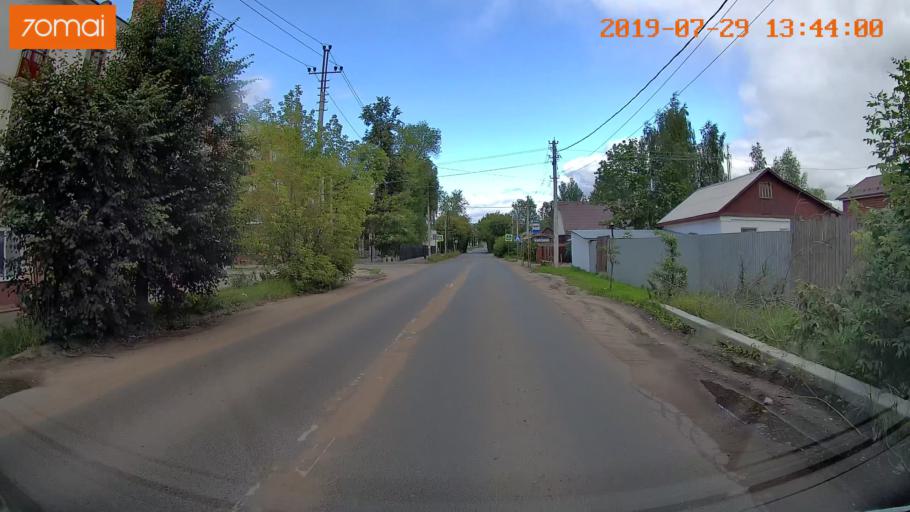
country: RU
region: Ivanovo
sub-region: Gorod Ivanovo
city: Ivanovo
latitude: 57.0080
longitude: 40.9304
